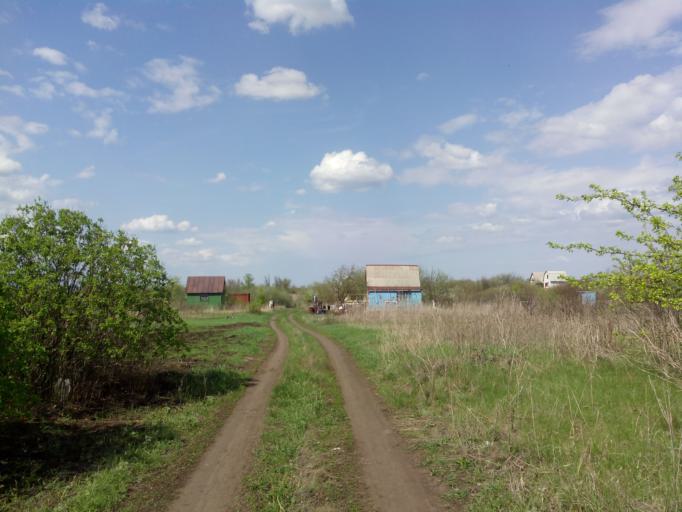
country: RU
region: Voronezj
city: Borisoglebsk
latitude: 51.3751
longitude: 42.1488
